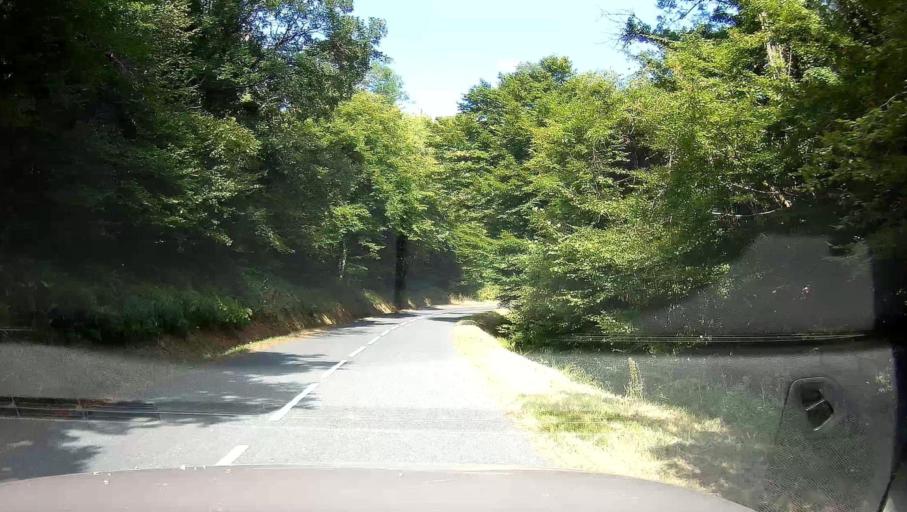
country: FR
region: Rhone-Alpes
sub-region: Departement du Rhone
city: Cogny
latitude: 45.9858
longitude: 4.5738
